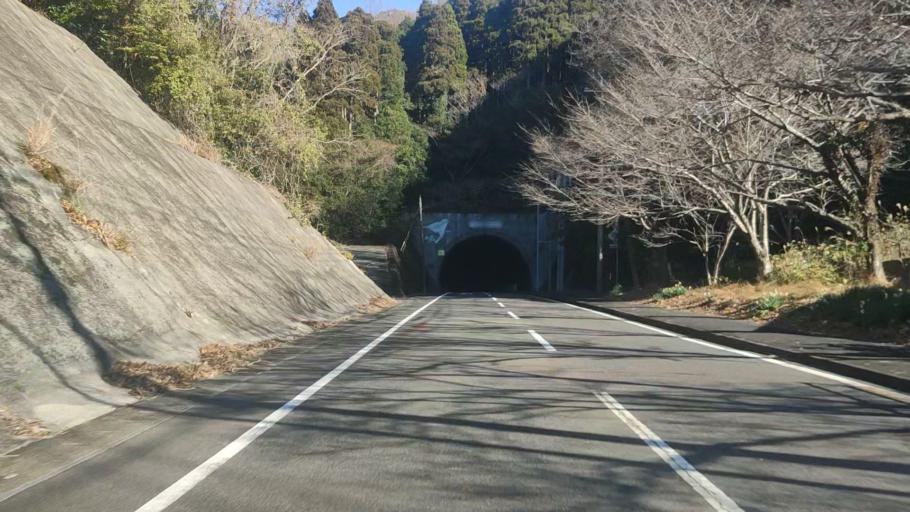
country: JP
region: Miyazaki
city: Nobeoka
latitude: 32.6907
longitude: 131.8099
